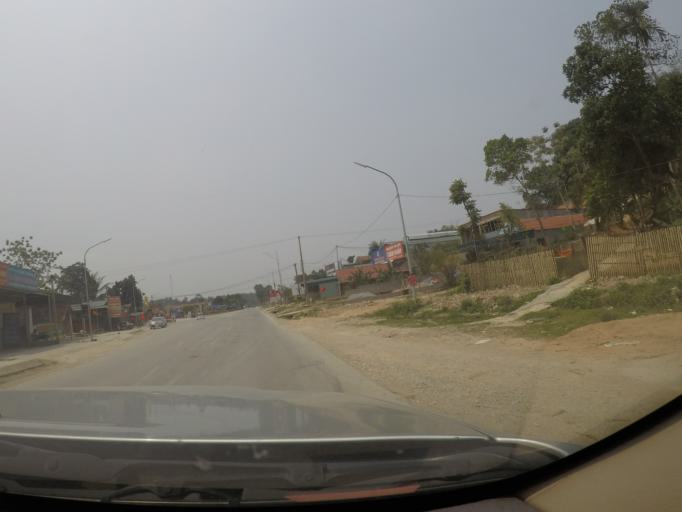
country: VN
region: Thanh Hoa
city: Thi Tran Yen Cat
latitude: 19.6690
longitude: 105.4478
